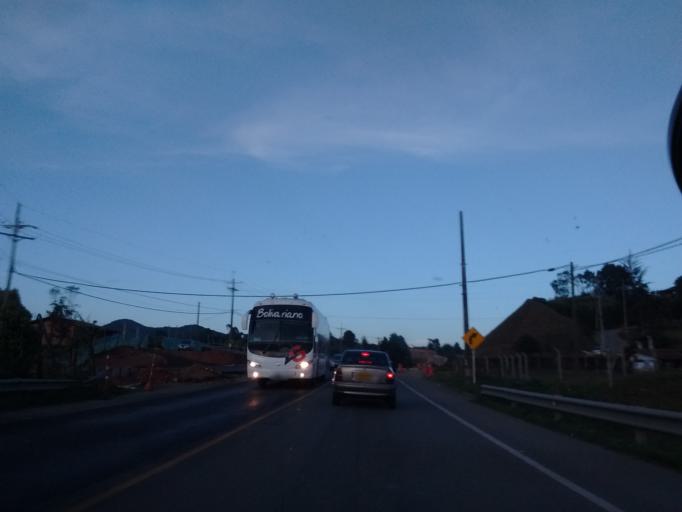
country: CO
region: Antioquia
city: Santuario
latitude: 6.1410
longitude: -75.3026
